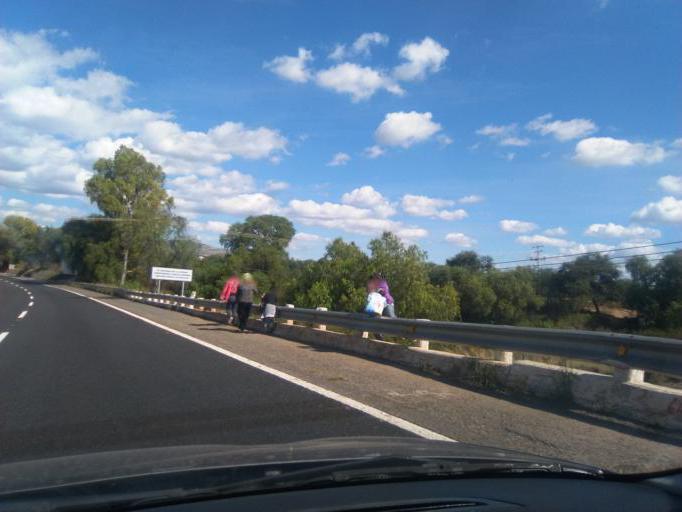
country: MX
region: Guanajuato
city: Santa Teresa
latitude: 20.9685
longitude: -101.3126
